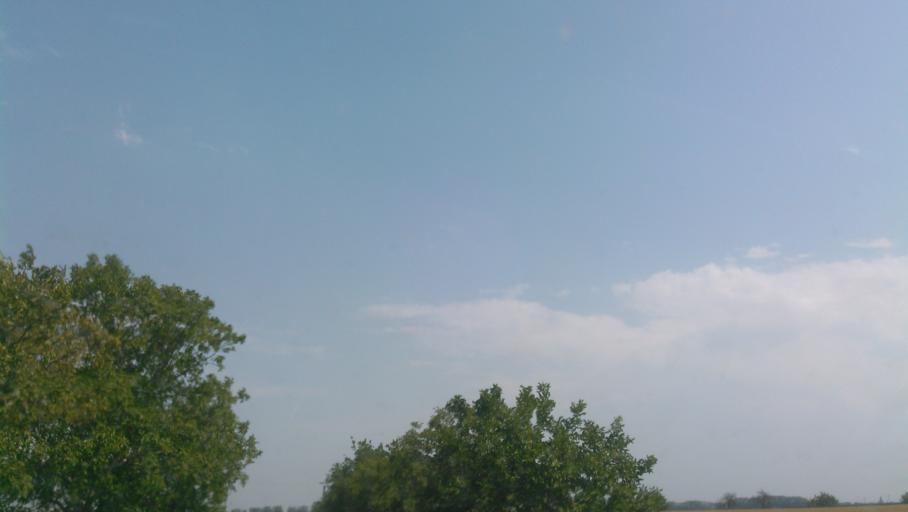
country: SK
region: Trnavsky
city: Dunajska Streda
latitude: 48.0325
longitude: 17.5408
